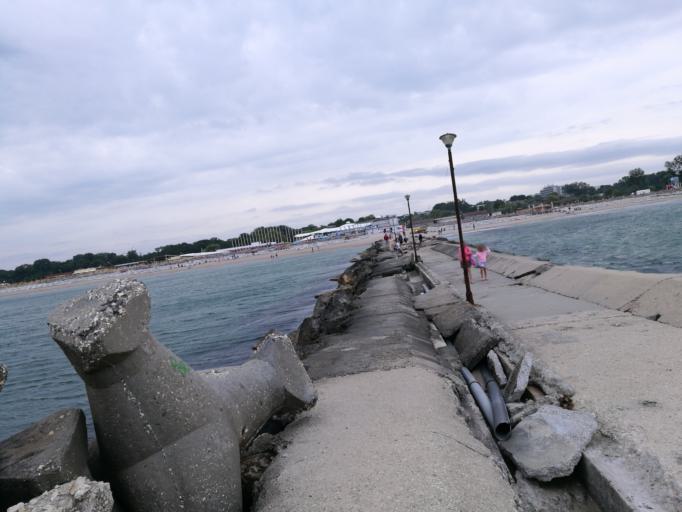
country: RO
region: Constanta
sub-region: Comuna Douazeci si Trei August
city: Douazeci si Trei August
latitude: 43.8669
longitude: 28.6085
